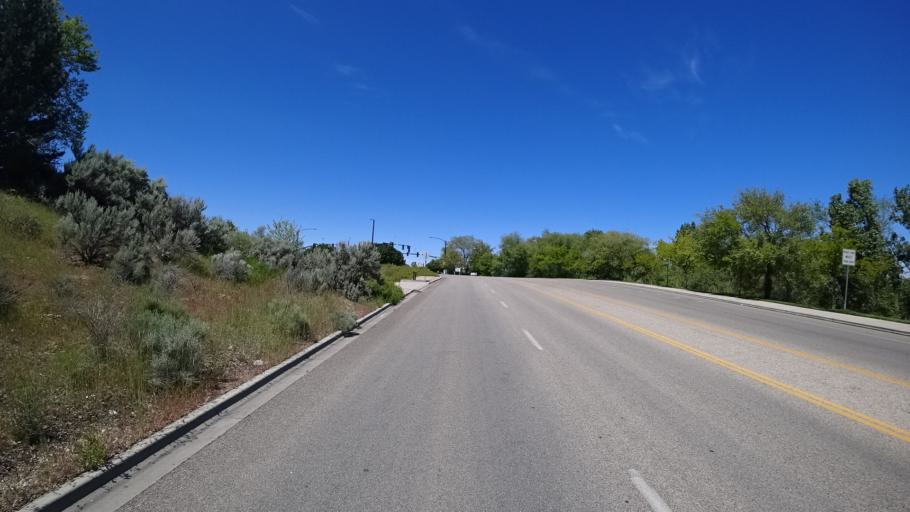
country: US
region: Idaho
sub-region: Ada County
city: Boise
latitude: 43.5682
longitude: -116.1810
